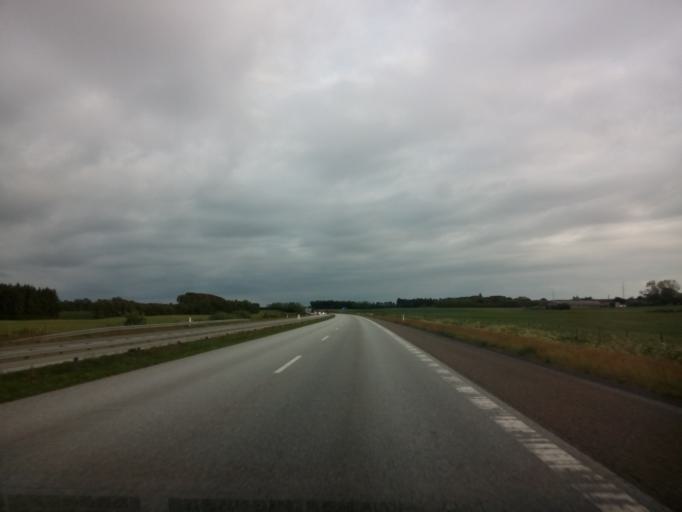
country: DK
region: North Denmark
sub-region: Hjorring Kommune
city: Vra
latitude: 57.3754
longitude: 10.0217
